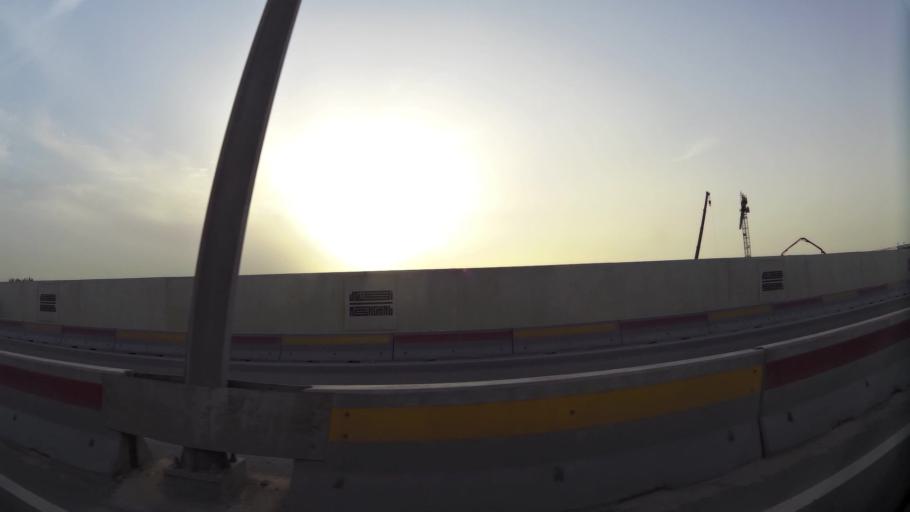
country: QA
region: Baladiyat ad Dawhah
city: Doha
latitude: 25.3510
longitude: 51.5211
